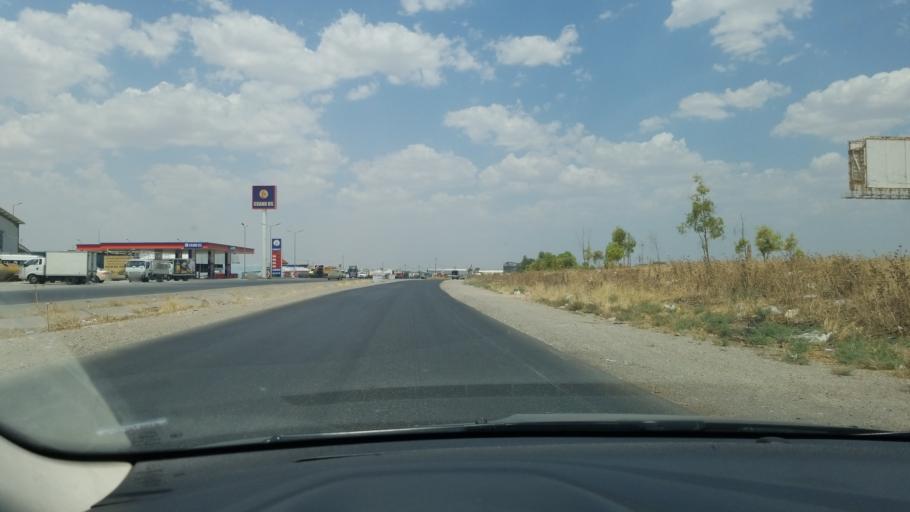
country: IQ
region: Arbil
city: Erbil
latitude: 36.0922
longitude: 44.0228
